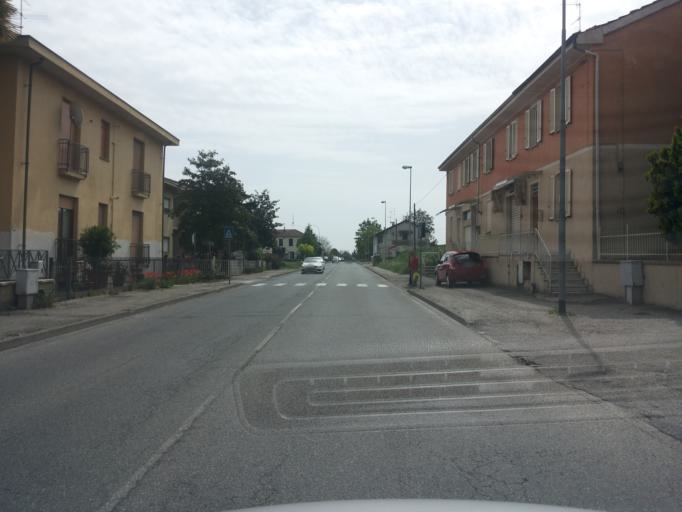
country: IT
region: Piedmont
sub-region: Provincia di Alessandria
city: Terruggia
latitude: 45.0977
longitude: 8.4564
